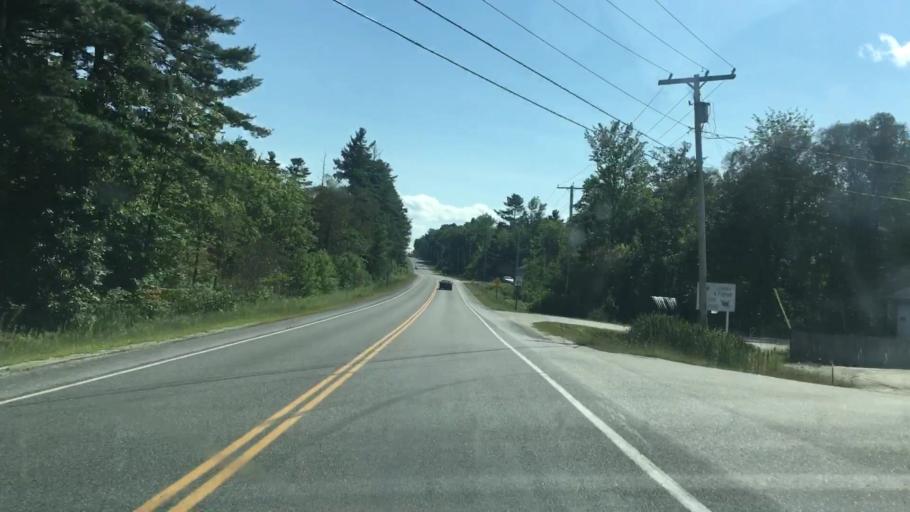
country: US
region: Maine
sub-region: Androscoggin County
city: Lisbon
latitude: 44.0711
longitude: -70.0824
